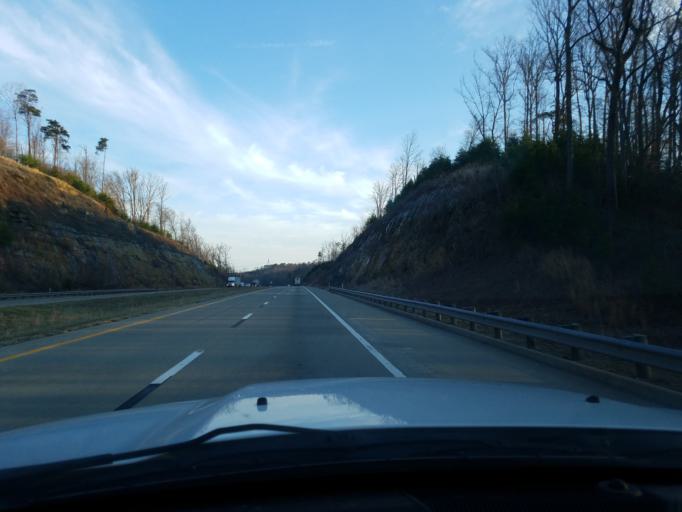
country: US
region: West Virginia
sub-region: Putnam County
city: Eleanor
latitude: 38.4958
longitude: -81.9323
